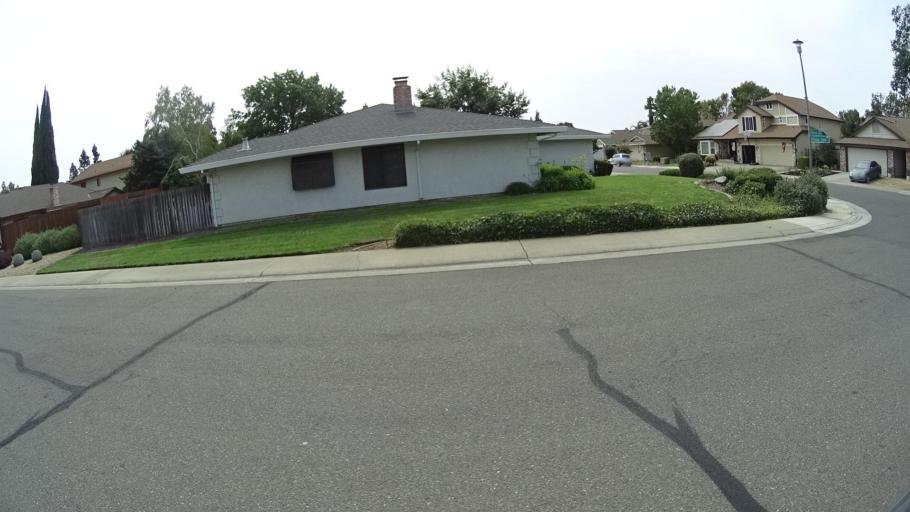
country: US
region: California
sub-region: Sacramento County
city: Elk Grove
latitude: 38.4194
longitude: -121.3892
